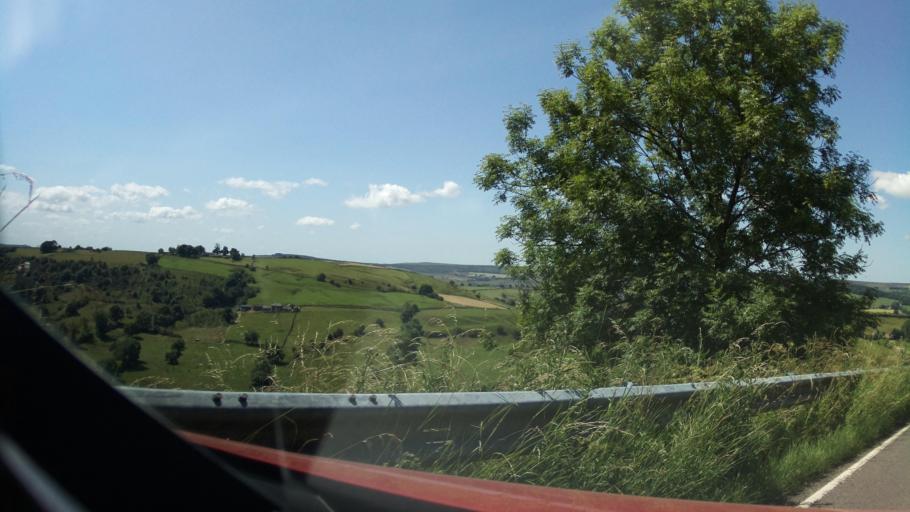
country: GB
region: England
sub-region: Derbyshire
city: Buxton
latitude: 53.1816
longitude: -1.8420
